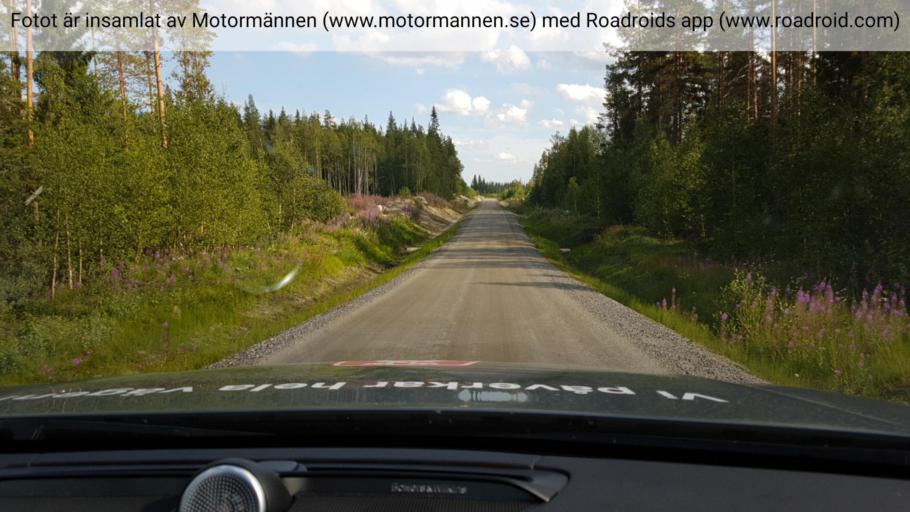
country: SE
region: Vaesterbotten
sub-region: Dorotea Kommun
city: Dorotea
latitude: 63.9390
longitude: 16.0897
